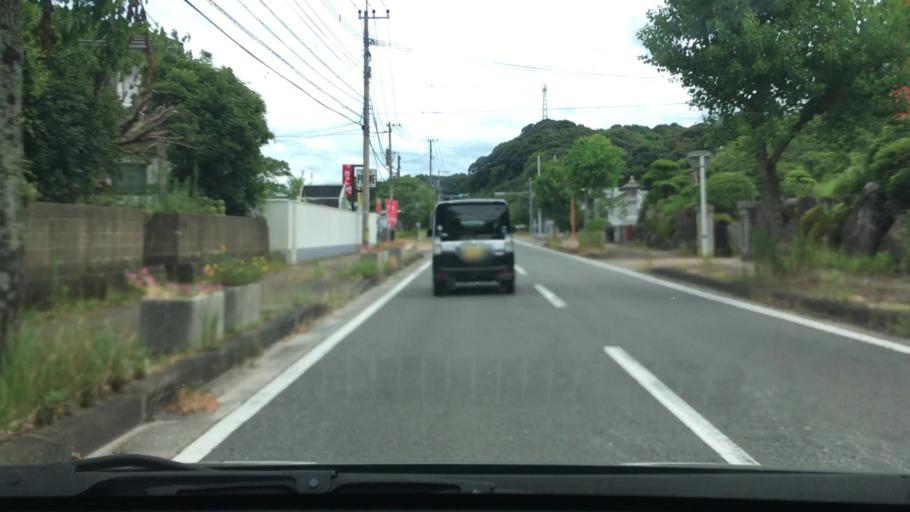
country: JP
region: Nagasaki
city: Sasebo
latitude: 32.9895
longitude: 129.7656
